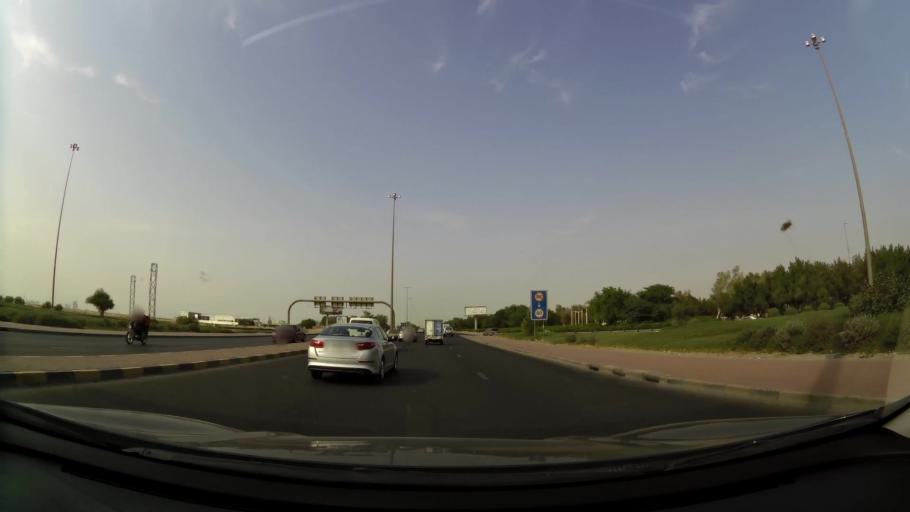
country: KW
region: Al Farwaniyah
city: Al Farwaniyah
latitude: 29.3043
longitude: 47.9634
